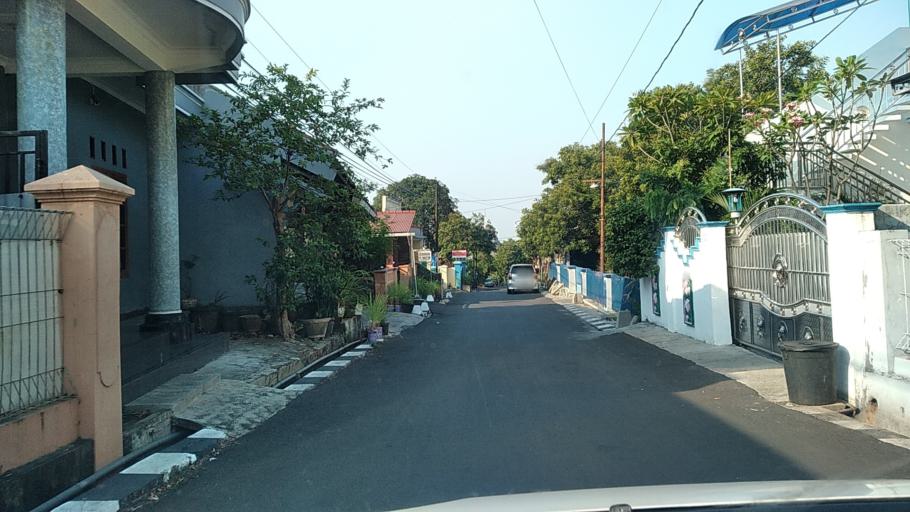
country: ID
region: Central Java
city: Ungaran
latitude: -7.0681
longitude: 110.4284
